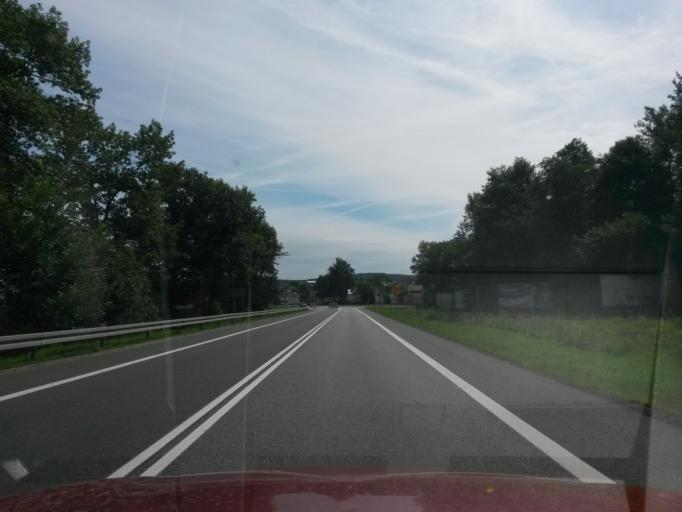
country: PL
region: Lesser Poland Voivodeship
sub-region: Powiat bochenski
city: Lapczyca
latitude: 49.9613
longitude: 20.3618
